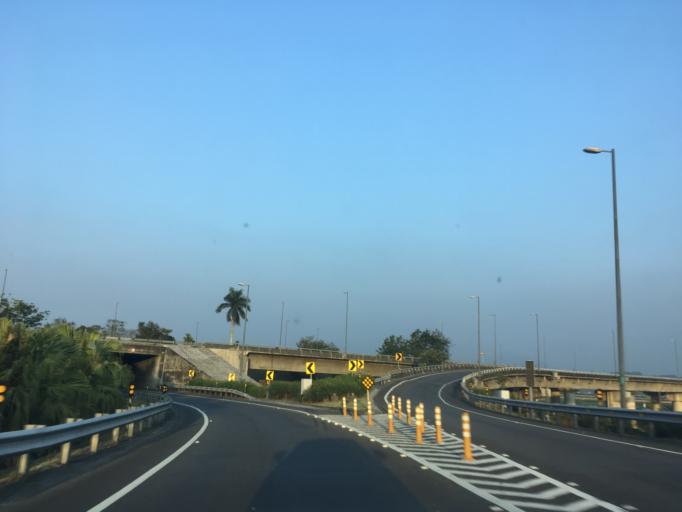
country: TW
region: Taiwan
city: Zhongxing New Village
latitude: 23.9470
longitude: 120.6684
